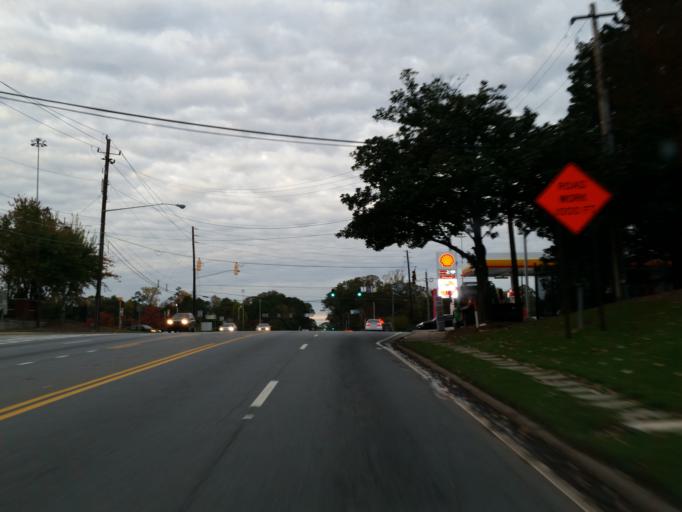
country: US
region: Georgia
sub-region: Fulton County
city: Atlanta
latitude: 33.8006
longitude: -84.4078
